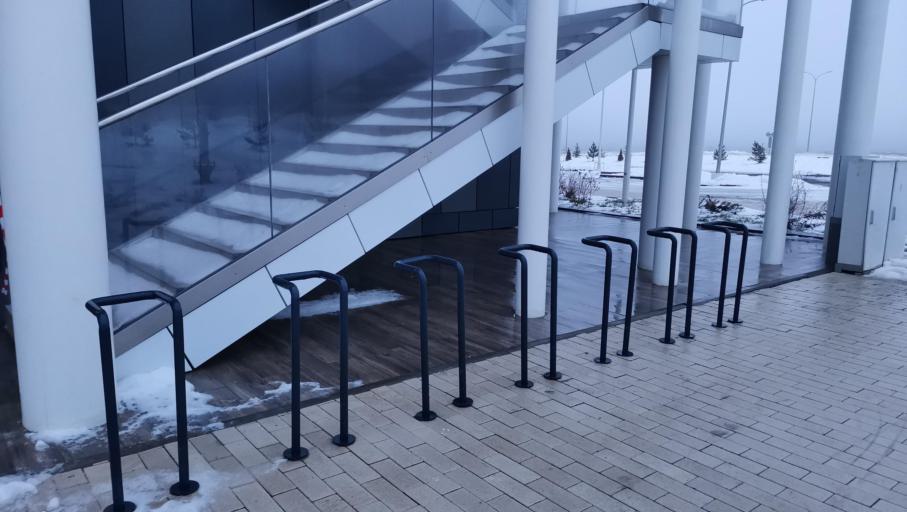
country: RU
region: Tatarstan
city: Sviyazhsk
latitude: 55.7442
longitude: 48.7482
